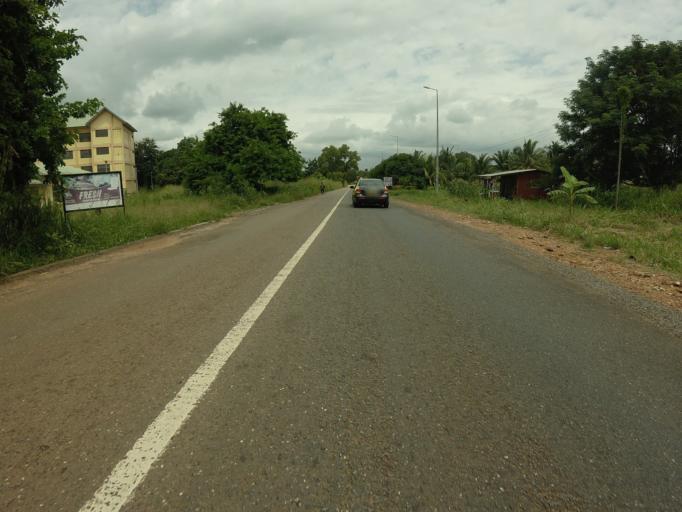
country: GH
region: Volta
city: Ho
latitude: 6.5864
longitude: 0.4630
